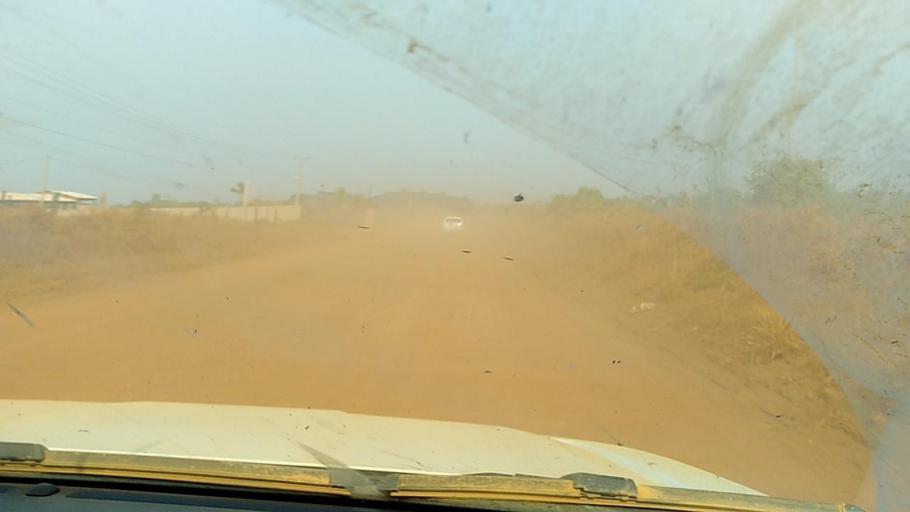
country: BR
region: Rondonia
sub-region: Porto Velho
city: Porto Velho
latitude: -8.7600
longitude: -63.9738
